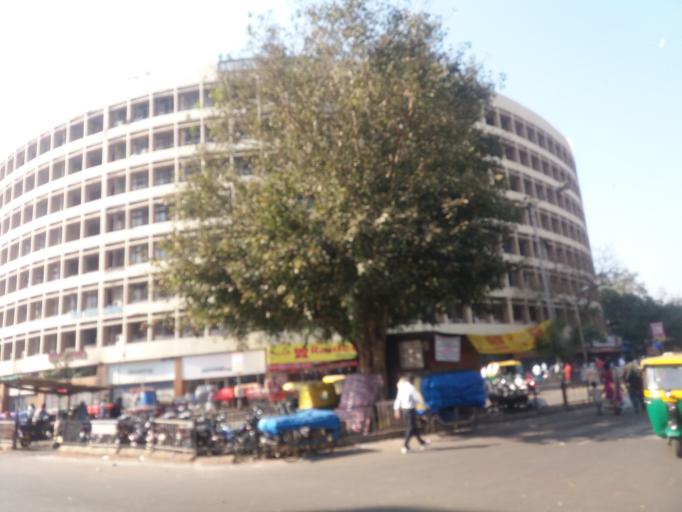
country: IN
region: Gujarat
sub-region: Ahmadabad
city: Ahmedabad
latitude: 23.0249
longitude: 72.5806
